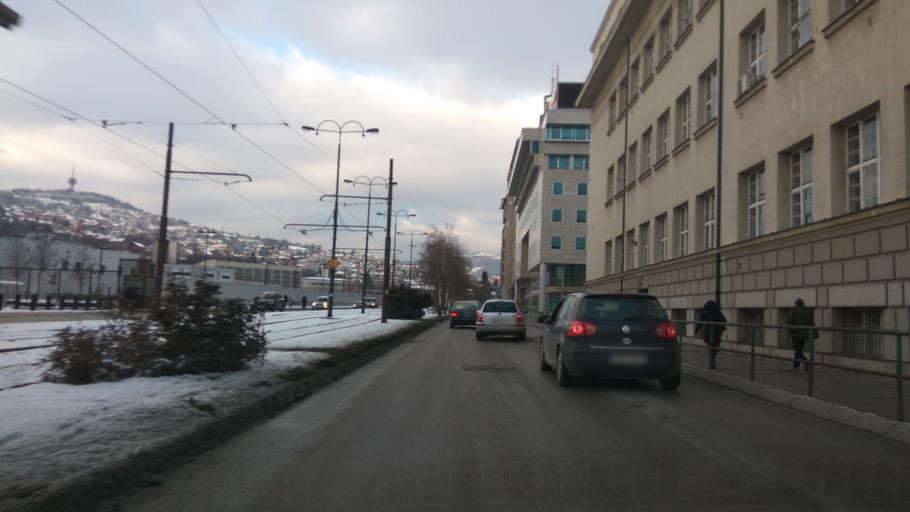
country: BA
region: Federation of Bosnia and Herzegovina
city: Kobilja Glava
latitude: 43.8562
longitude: 18.4015
